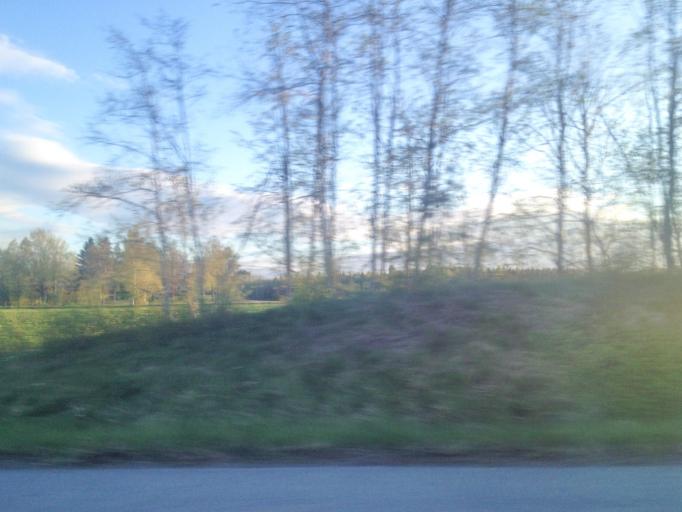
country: FI
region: Haeme
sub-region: Haemeenlinna
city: Janakkala
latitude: 60.8636
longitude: 24.5837
